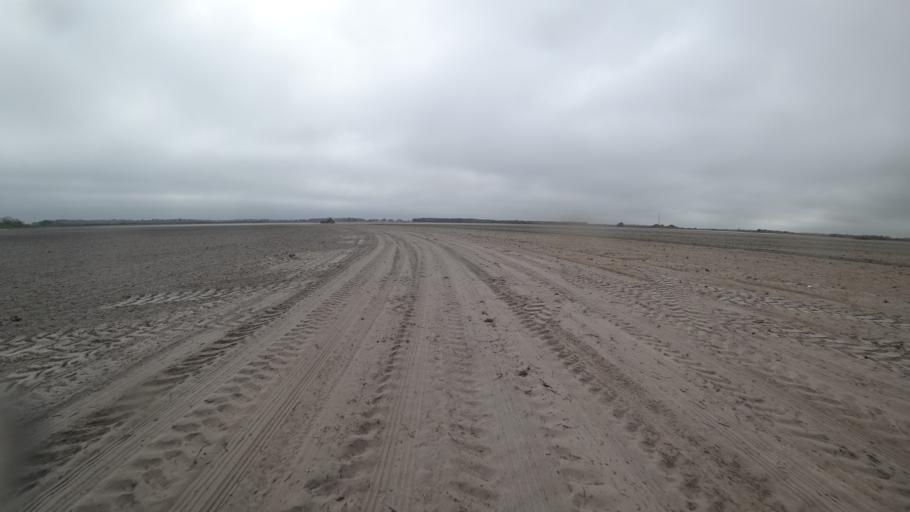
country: US
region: Florida
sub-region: Sarasota County
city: Warm Mineral Springs
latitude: 27.2930
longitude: -82.1767
